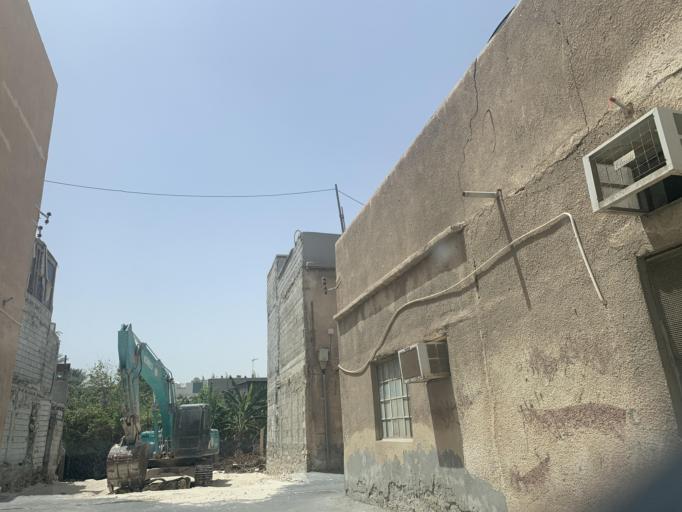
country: BH
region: Manama
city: Jidd Hafs
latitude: 26.2036
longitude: 50.5367
